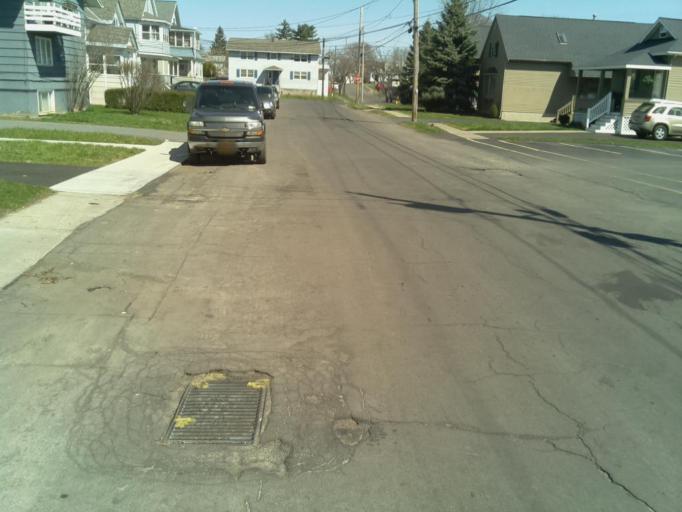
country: US
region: New York
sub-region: Onondaga County
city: Lyncourt
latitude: 43.0692
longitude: -76.1120
